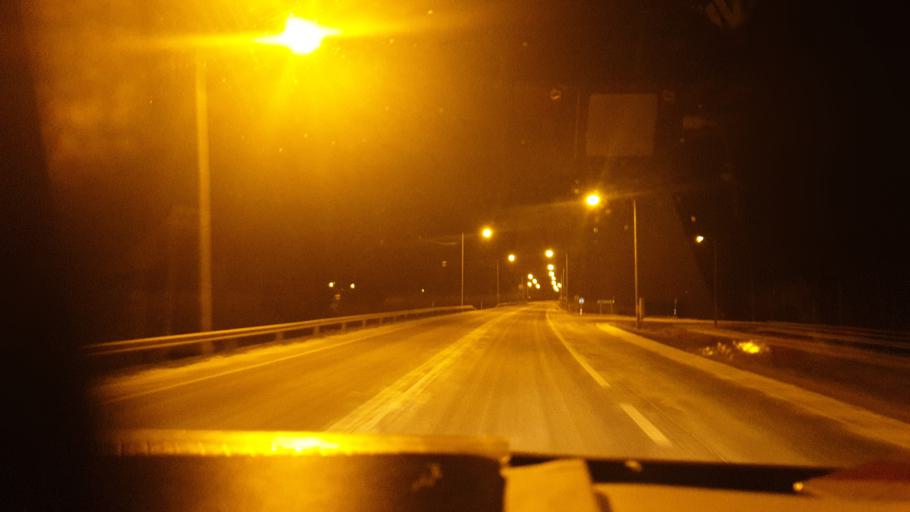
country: FI
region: Southern Ostrobothnia
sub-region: Kuusiokunnat
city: Alavus
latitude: 62.5965
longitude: 23.6613
